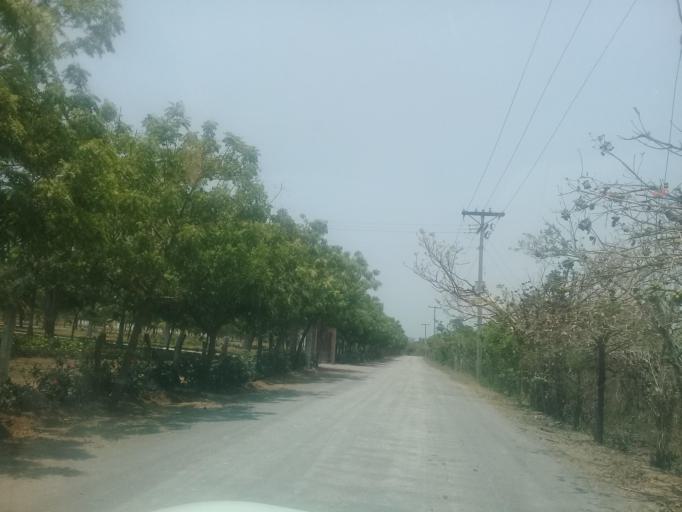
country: MX
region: Veracruz
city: Jamapa
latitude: 19.0846
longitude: -96.2366
